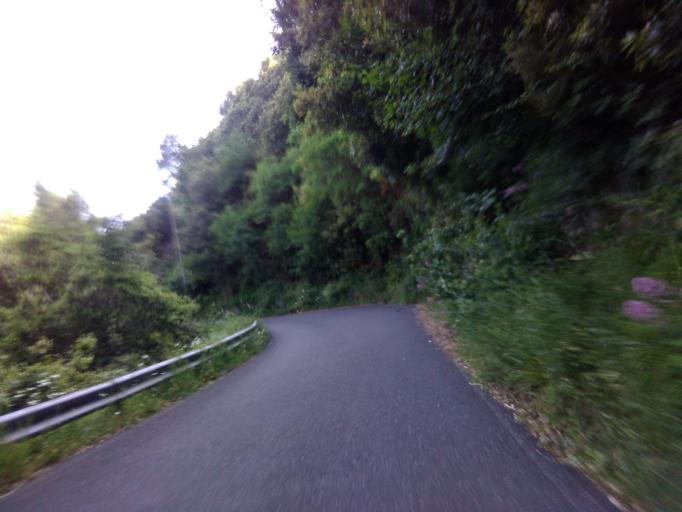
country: IT
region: Tuscany
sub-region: Provincia di Massa-Carrara
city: Fosdinovo
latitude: 44.1626
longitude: 9.9996
